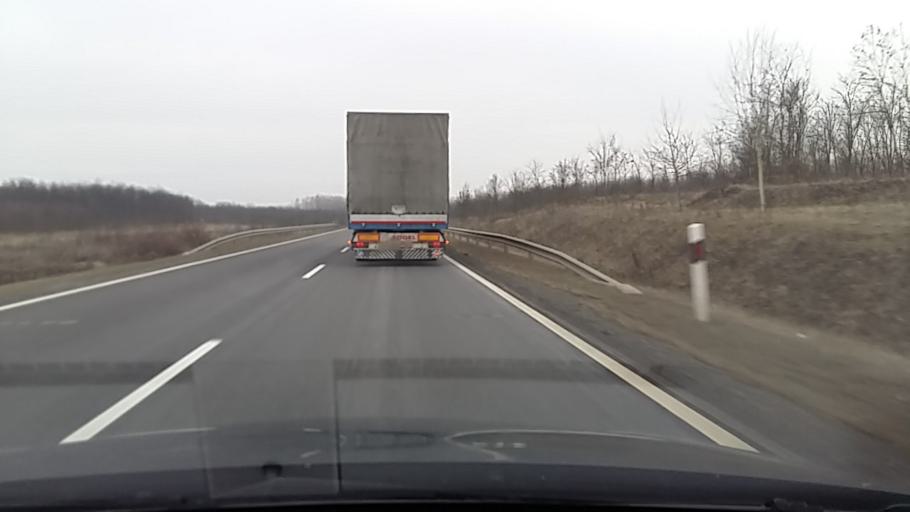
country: HU
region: Szabolcs-Szatmar-Bereg
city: Nagykallo
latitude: 47.9205
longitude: 21.8196
